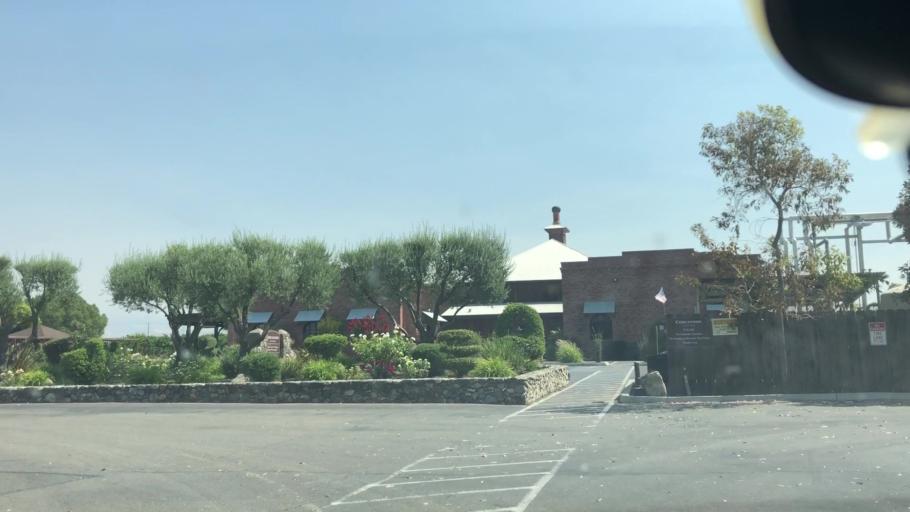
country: US
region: California
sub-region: Alameda County
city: Livermore
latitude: 37.6676
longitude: -121.7400
